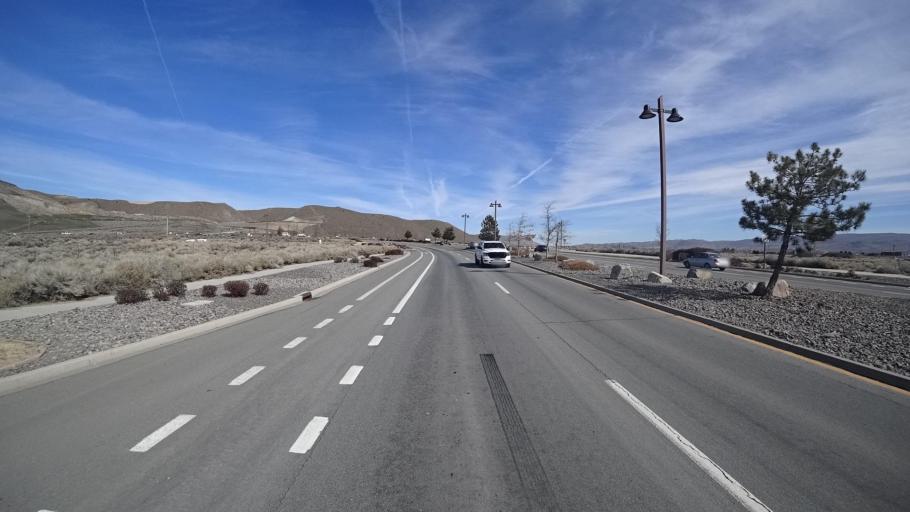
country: US
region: Nevada
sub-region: Washoe County
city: Sun Valley
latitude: 39.6061
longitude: -119.7301
